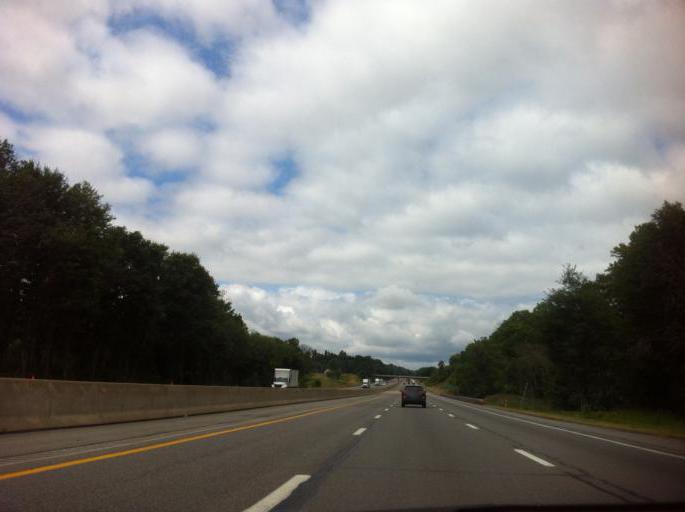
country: US
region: Ohio
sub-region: Portage County
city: Streetsboro
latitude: 41.2480
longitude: -81.2808
